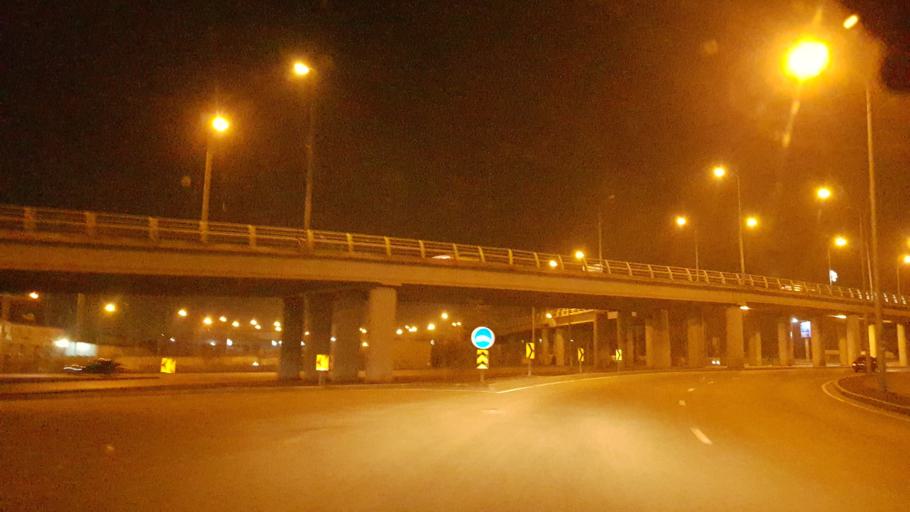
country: KZ
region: Almaty Qalasy
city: Almaty
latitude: 43.2728
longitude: 76.8862
